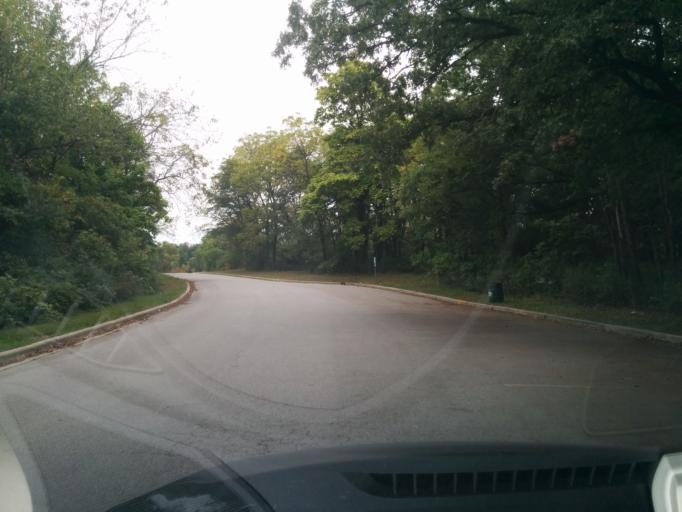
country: US
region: Illinois
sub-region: Cook County
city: Palos Heights
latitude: 41.6482
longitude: -87.7914
